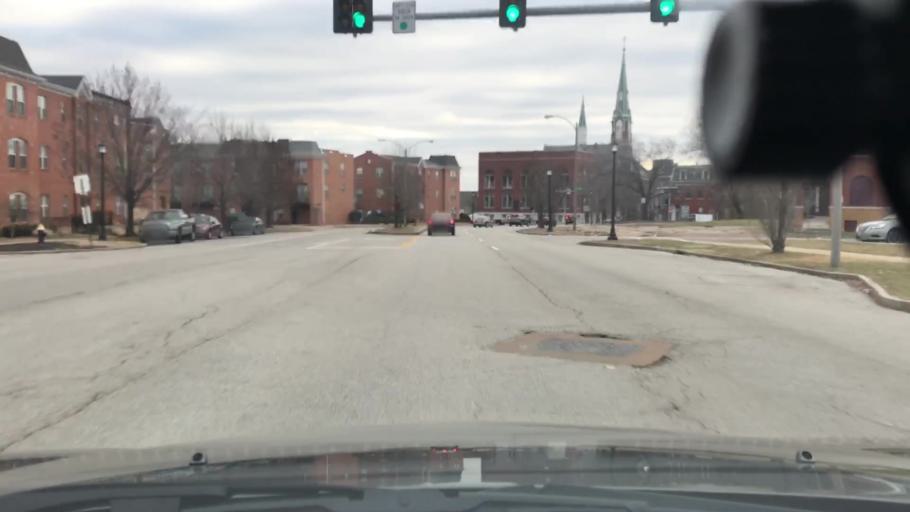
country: US
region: Missouri
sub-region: City of Saint Louis
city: St. Louis
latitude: 38.6132
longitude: -90.2079
